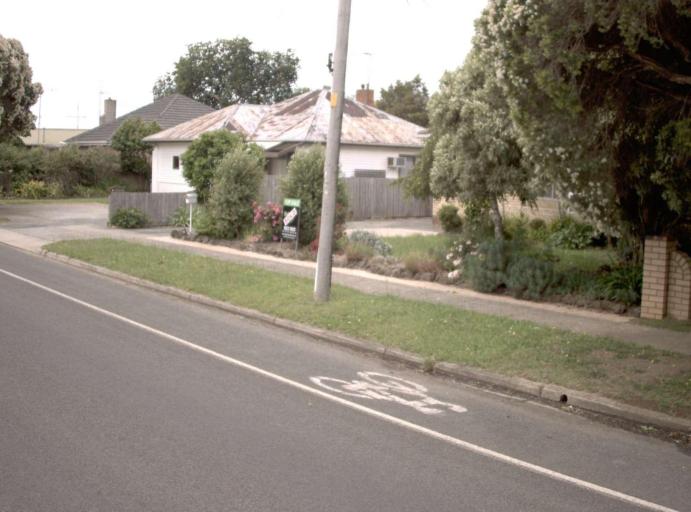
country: AU
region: Victoria
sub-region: Baw Baw
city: Warragul
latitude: -38.1451
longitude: 145.9379
